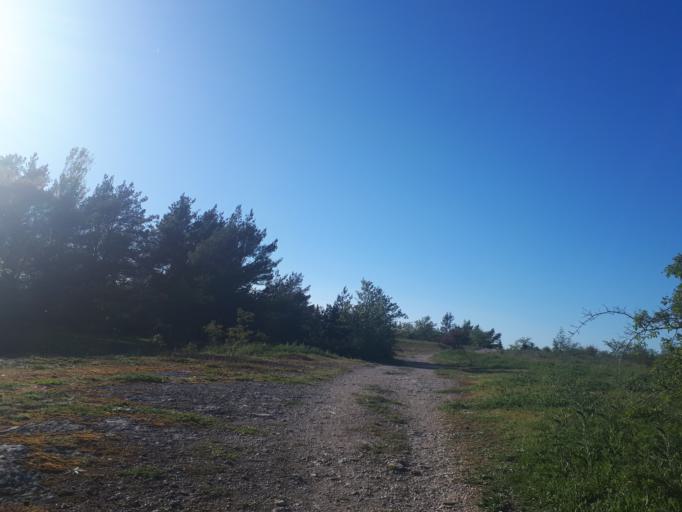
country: SE
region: Gotland
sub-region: Gotland
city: Vibble
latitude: 57.6117
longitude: 18.2513
